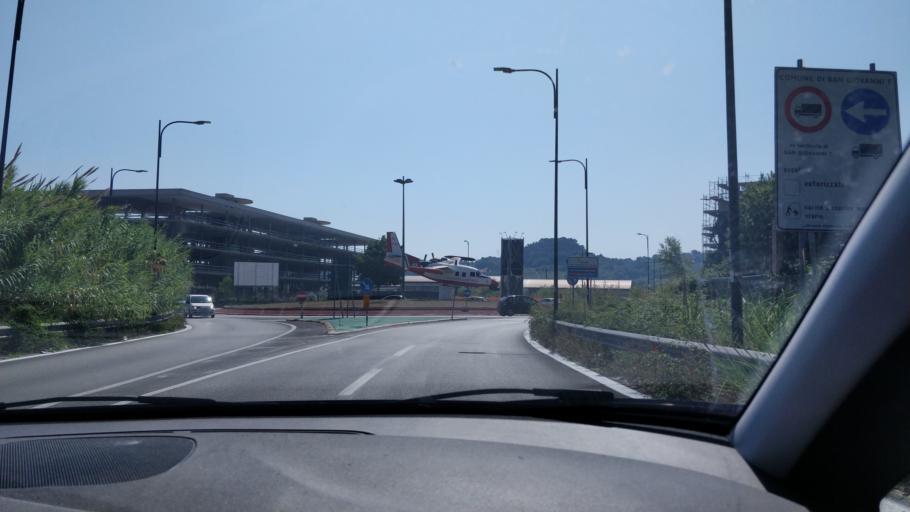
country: IT
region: Abruzzo
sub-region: Provincia di Chieti
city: Sambuceto
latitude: 42.4392
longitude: 14.1950
